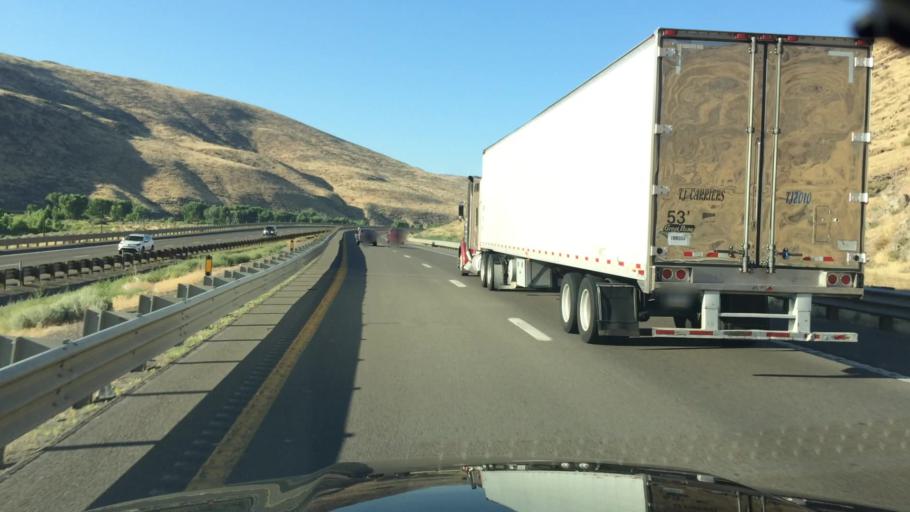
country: US
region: Nevada
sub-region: Lyon County
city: Fernley
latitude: 39.5748
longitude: -119.4726
